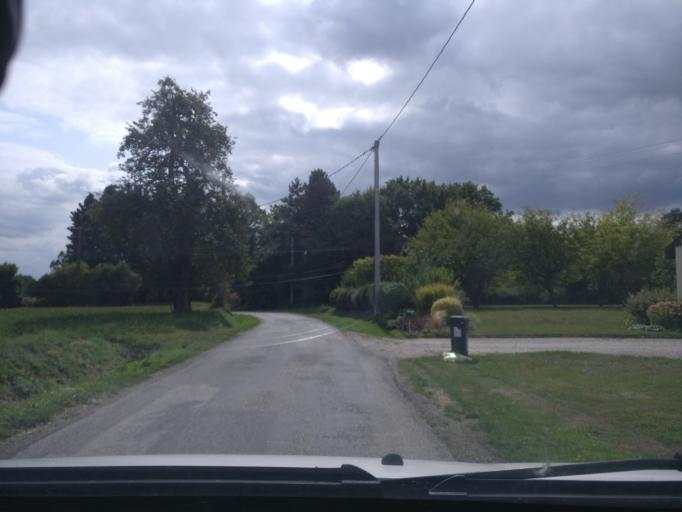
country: FR
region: Brittany
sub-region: Departement d'Ille-et-Vilaine
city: Noyal-sur-Vilaine
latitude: 48.0796
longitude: -1.5330
